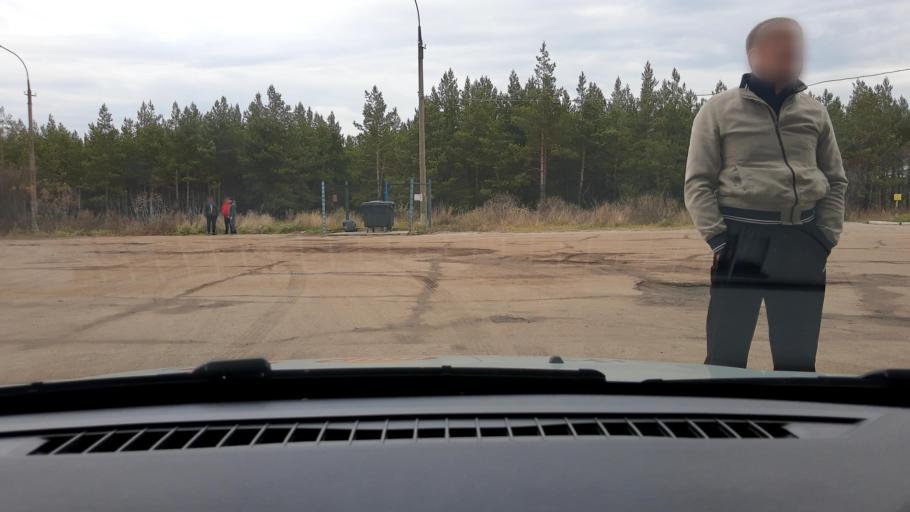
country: RU
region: Nizjnij Novgorod
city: Dzerzhinsk
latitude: 56.2779
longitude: 43.4789
